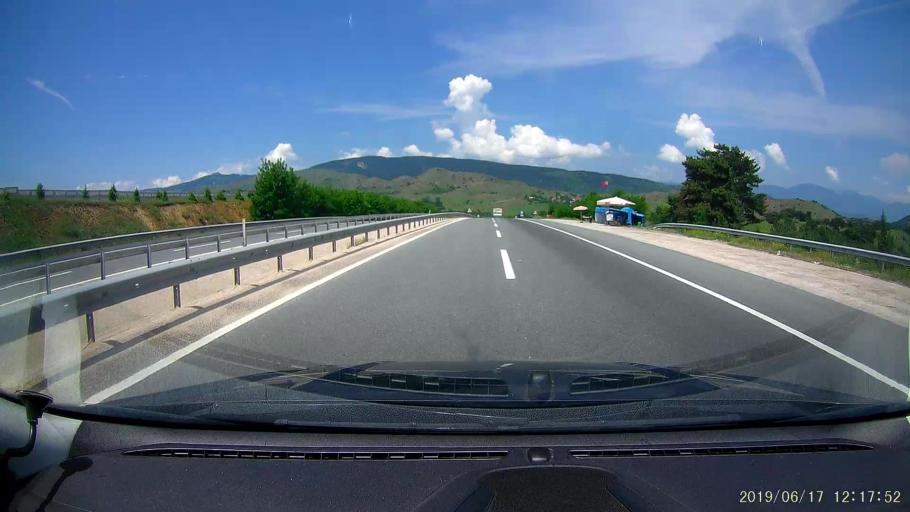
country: TR
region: Karabuk
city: Gozyeri
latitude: 40.8609
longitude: 32.5259
